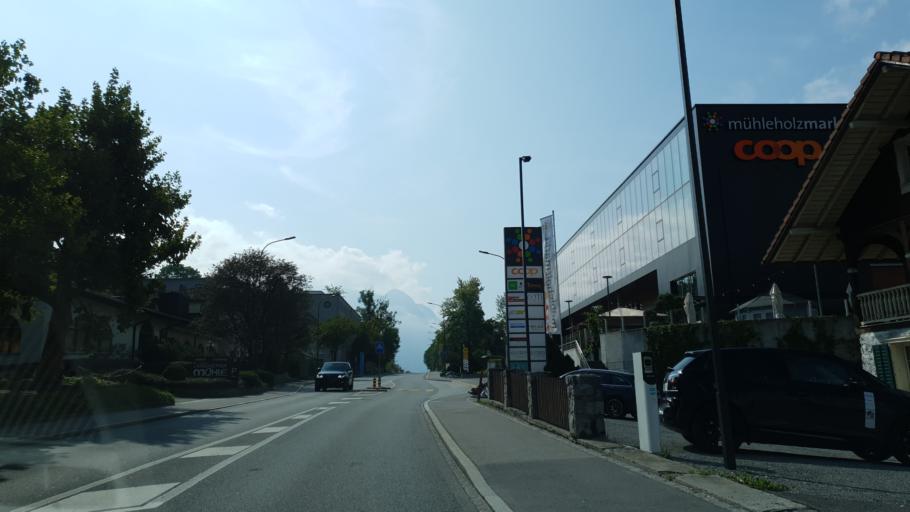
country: LI
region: Schaan
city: Schaan
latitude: 47.1553
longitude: 9.5103
